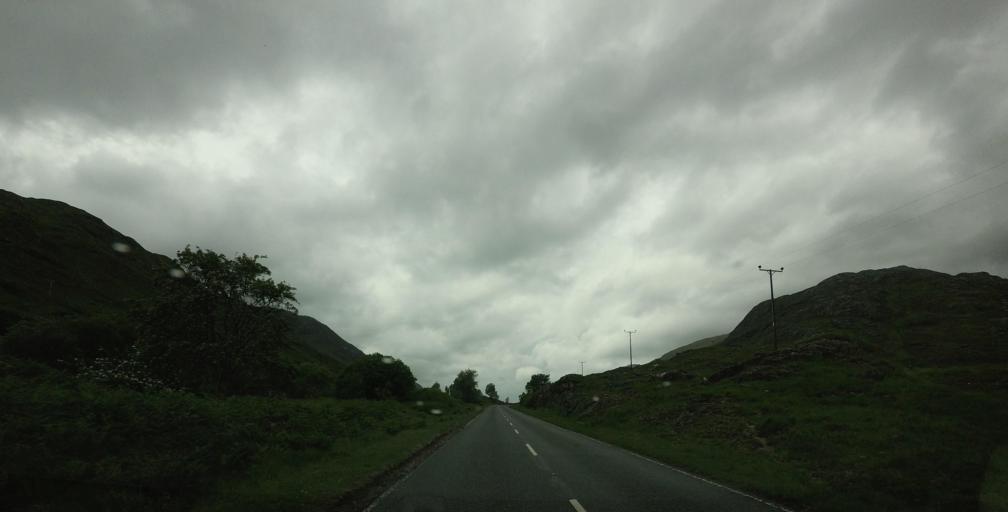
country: GB
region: Scotland
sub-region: Argyll and Bute
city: Oban
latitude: 56.6829
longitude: -5.3862
